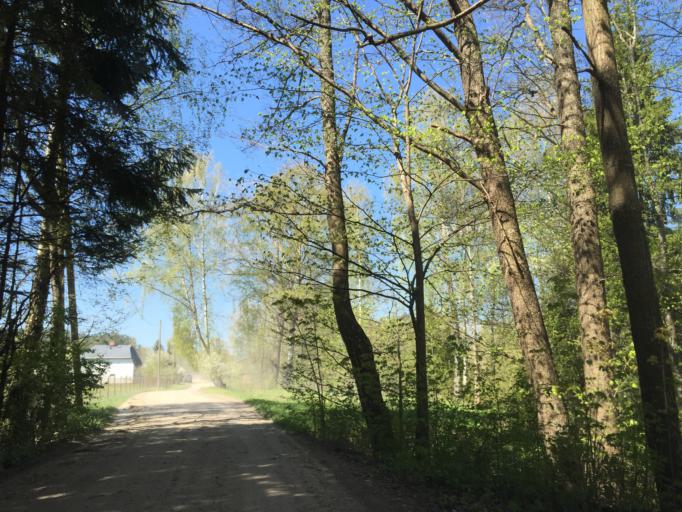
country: LV
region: Saulkrastu
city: Saulkrasti
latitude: 57.3187
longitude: 24.4349
